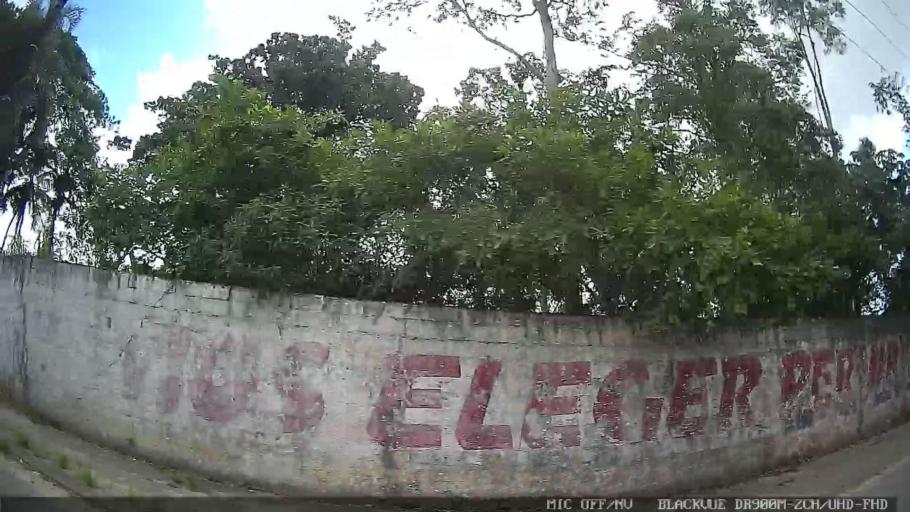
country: BR
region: Sao Paulo
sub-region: Peruibe
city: Peruibe
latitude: -24.3049
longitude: -47.0166
